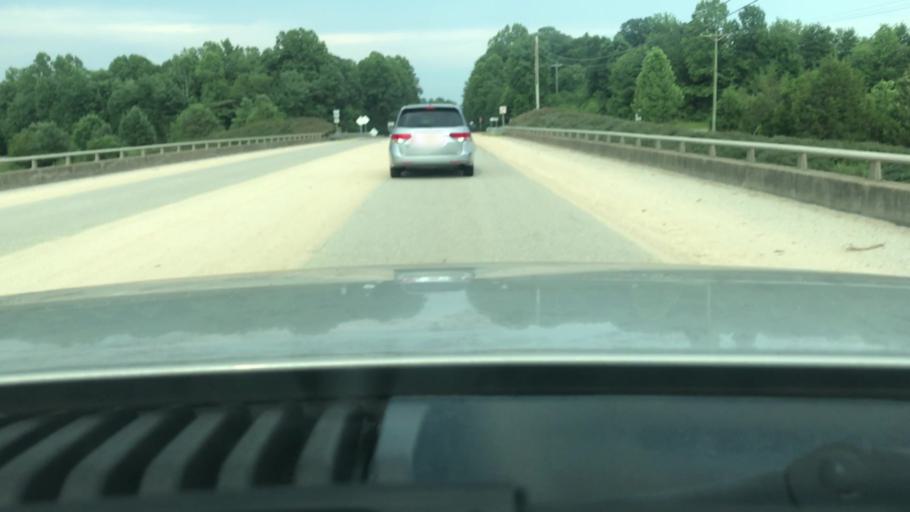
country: US
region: North Carolina
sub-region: Surry County
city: Elkin
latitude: 36.2802
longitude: -80.8221
